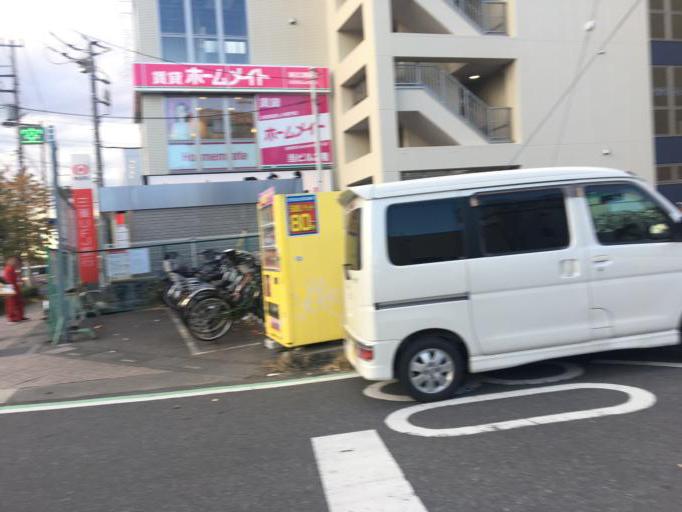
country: JP
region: Saitama
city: Koshigaya
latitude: 35.8759
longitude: 139.7444
